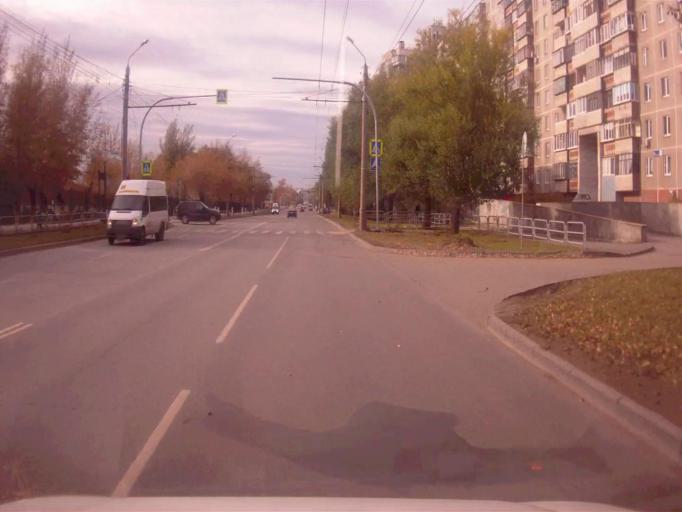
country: RU
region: Chelyabinsk
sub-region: Gorod Chelyabinsk
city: Chelyabinsk
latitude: 55.1126
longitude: 61.4625
